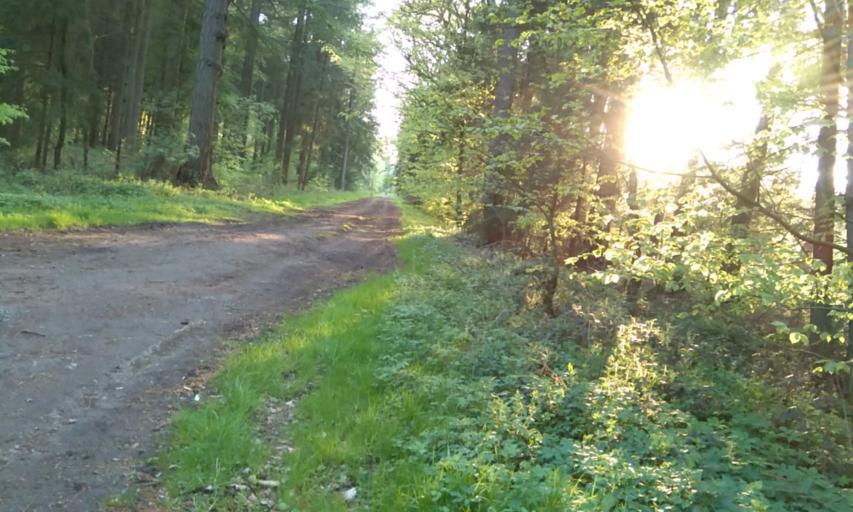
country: DE
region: Lower Saxony
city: Dollern
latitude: 53.5134
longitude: 9.5059
